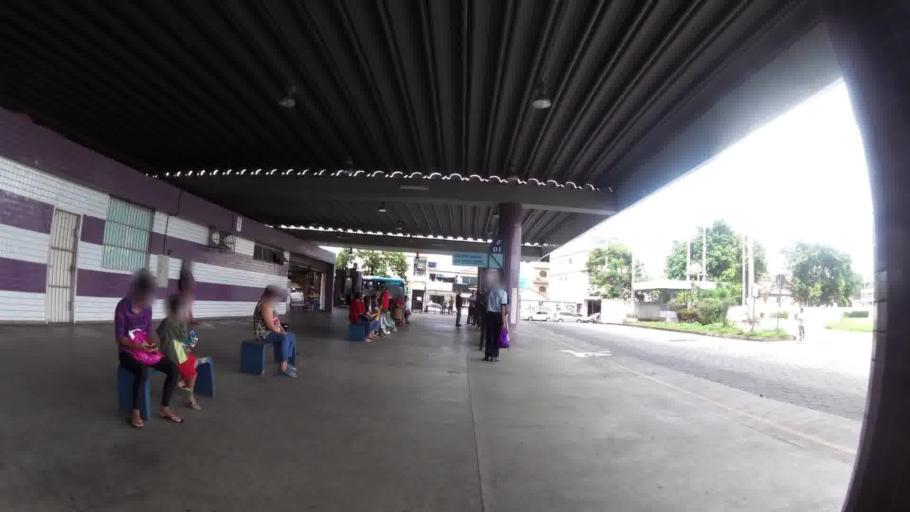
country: BR
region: Espirito Santo
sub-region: Vitoria
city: Vitoria
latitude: -20.3466
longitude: -40.3957
